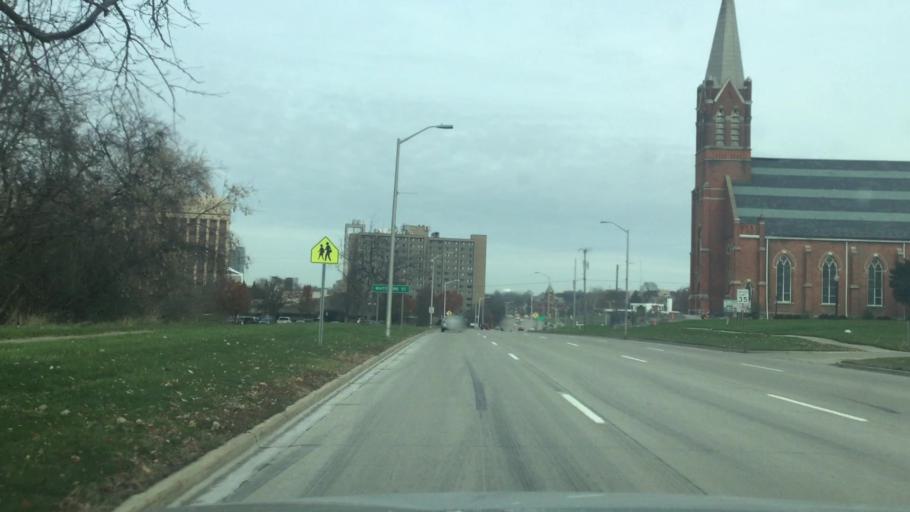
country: US
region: Michigan
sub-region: Oakland County
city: Pontiac
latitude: 42.6312
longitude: -83.2887
